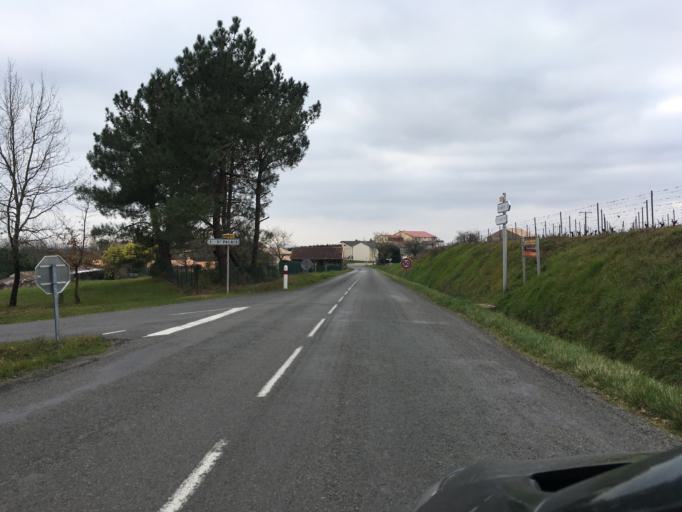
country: FR
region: Aquitaine
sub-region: Departement de la Gironde
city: Saint-Ciers-sur-Gironde
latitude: 45.3154
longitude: -0.5947
